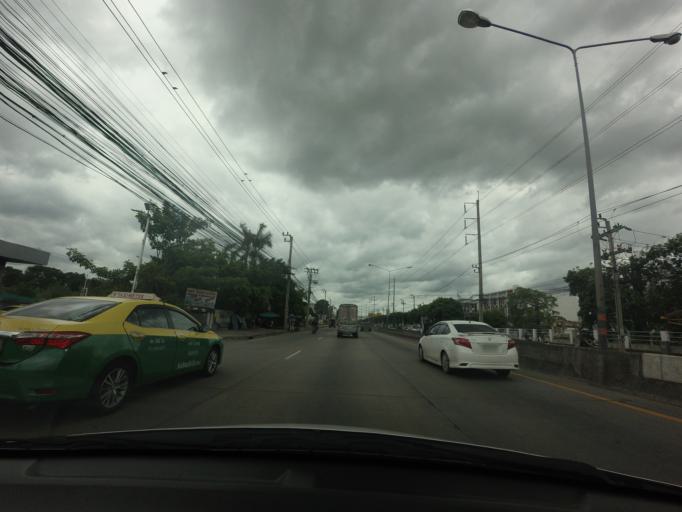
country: TH
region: Bangkok
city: Min Buri
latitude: 13.7755
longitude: 100.7463
